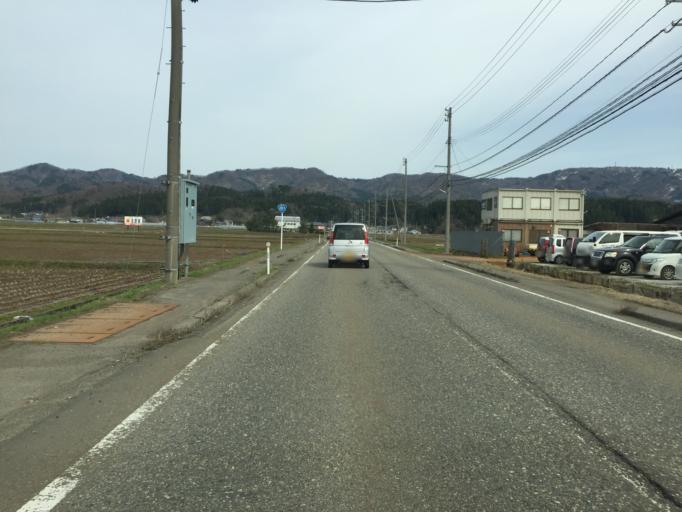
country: JP
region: Niigata
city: Nagaoka
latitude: 37.4545
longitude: 138.8889
